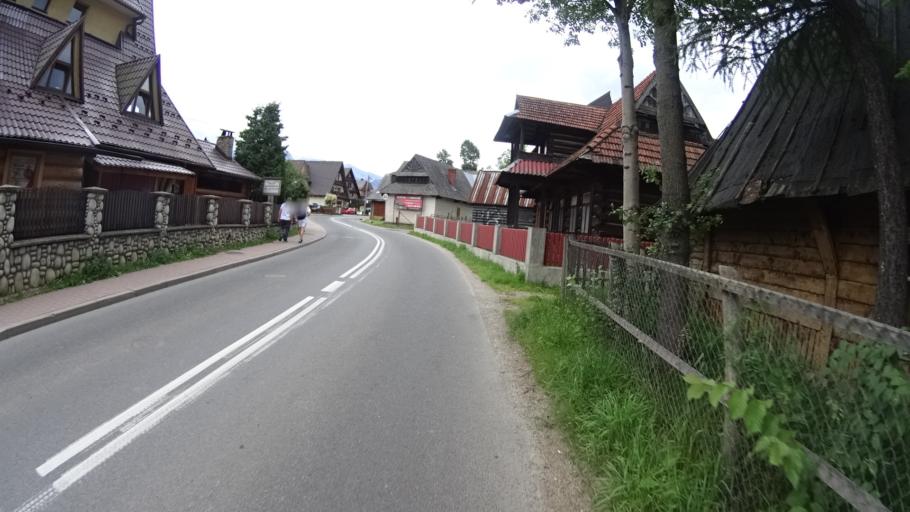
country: PL
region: Lesser Poland Voivodeship
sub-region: Powiat tatrzanski
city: Zakopane
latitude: 49.3130
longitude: 19.9740
